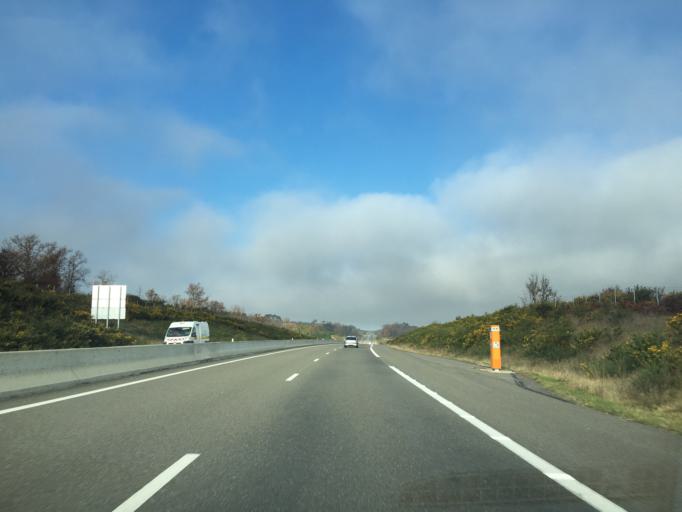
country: FR
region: Aquitaine
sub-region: Departement des Landes
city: Villeneuve-de-Marsan
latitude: 43.8029
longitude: -0.3024
